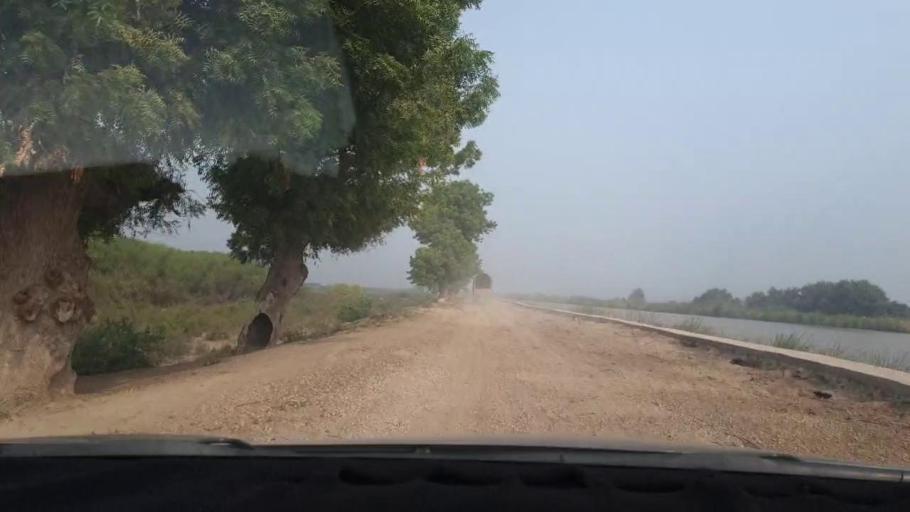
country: PK
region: Sindh
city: Matiari
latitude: 25.6520
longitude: 68.5614
